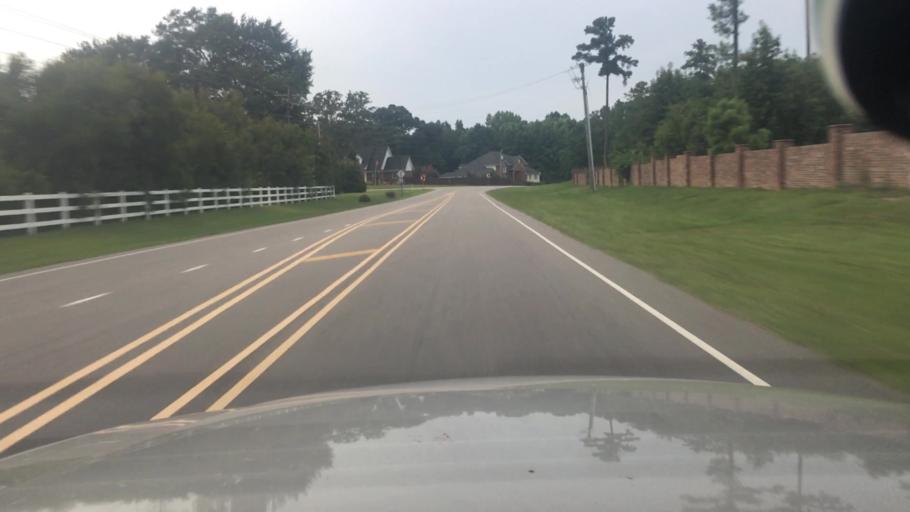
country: US
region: North Carolina
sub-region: Hoke County
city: Rockfish
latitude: 35.0011
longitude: -79.0256
